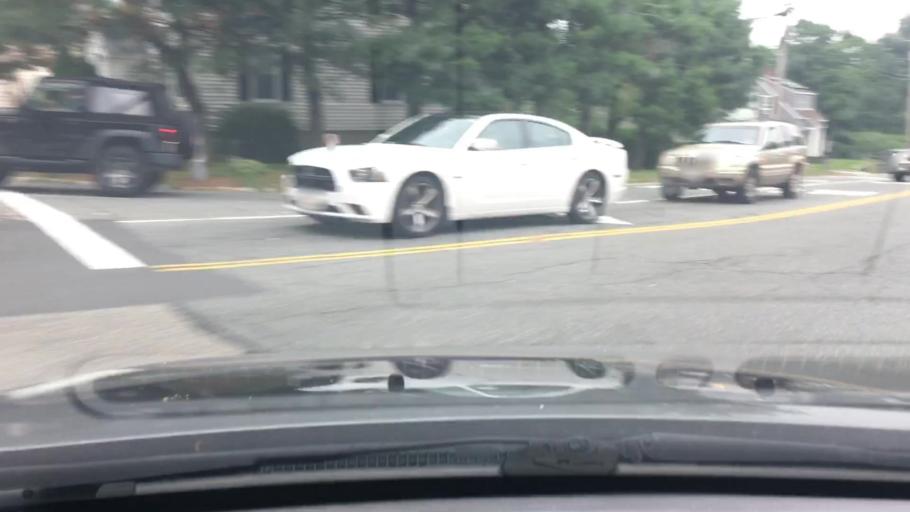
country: US
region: Massachusetts
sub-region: Worcester County
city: Milford
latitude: 42.1550
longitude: -71.5231
